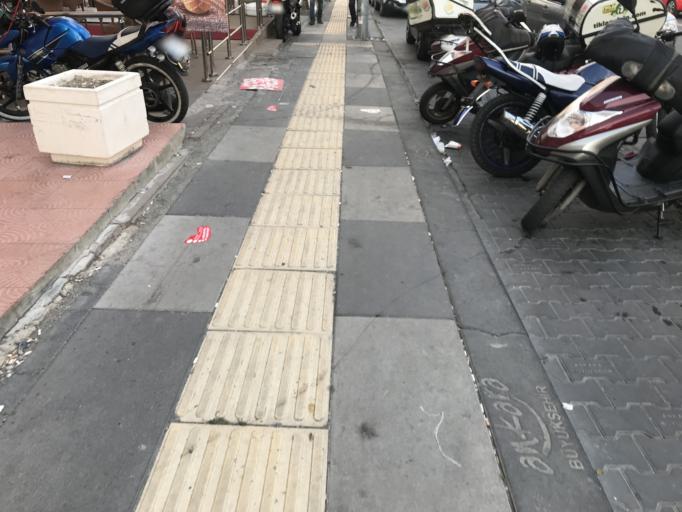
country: TR
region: Ankara
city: Ankara
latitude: 39.8731
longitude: 32.8329
